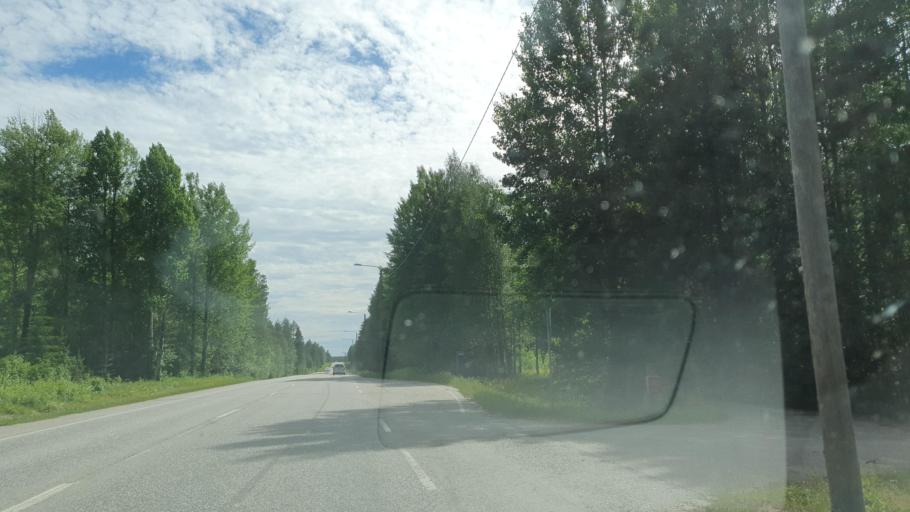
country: FI
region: Kainuu
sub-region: Kehys-Kainuu
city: Hyrynsalmi
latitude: 64.6684
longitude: 28.5062
